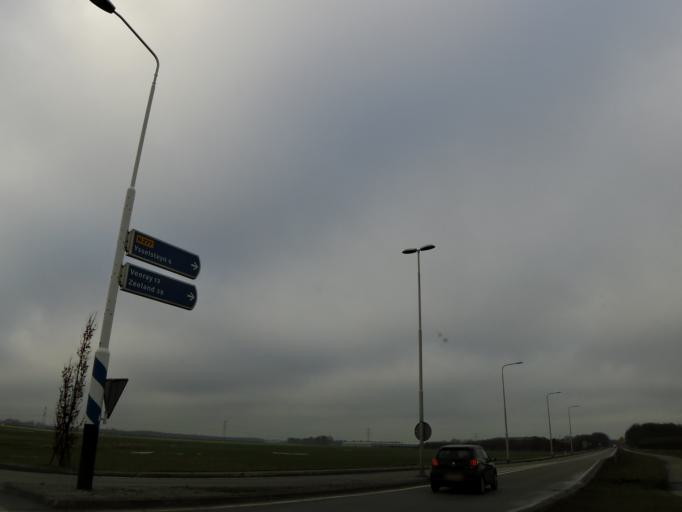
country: NL
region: Limburg
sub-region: Gemeente Venray
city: Venray
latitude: 51.4498
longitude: 5.9521
